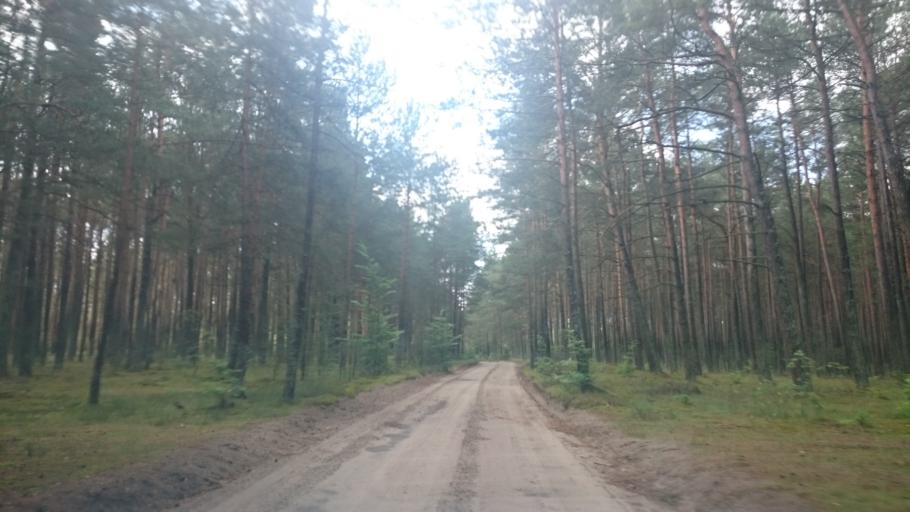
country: PL
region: Pomeranian Voivodeship
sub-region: Powiat koscierski
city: Karsin
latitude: 53.9883
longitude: 17.9326
